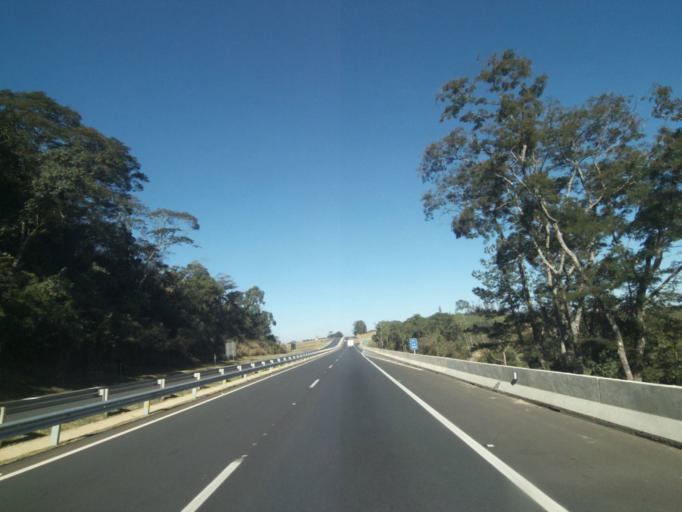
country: BR
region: Parana
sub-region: Tibagi
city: Tibagi
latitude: -24.8121
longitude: -50.4895
